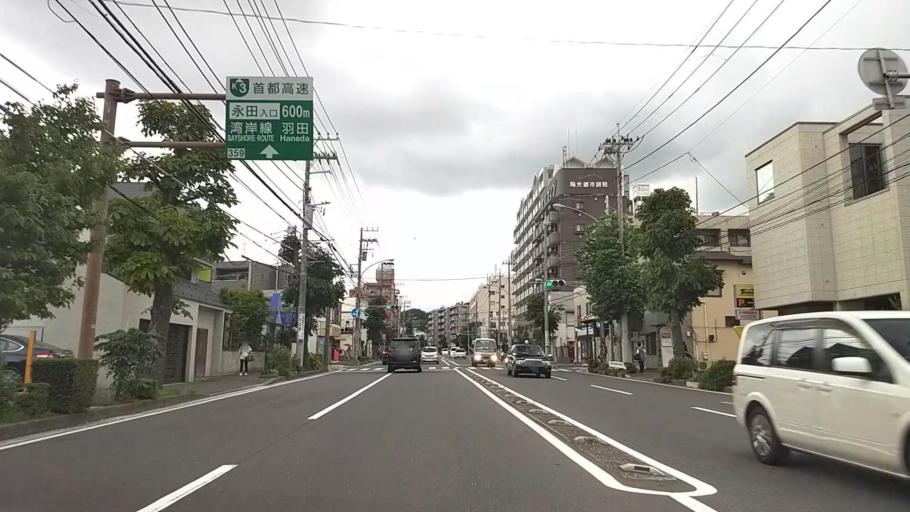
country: JP
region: Kanagawa
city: Yokohama
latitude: 35.4356
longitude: 139.6001
